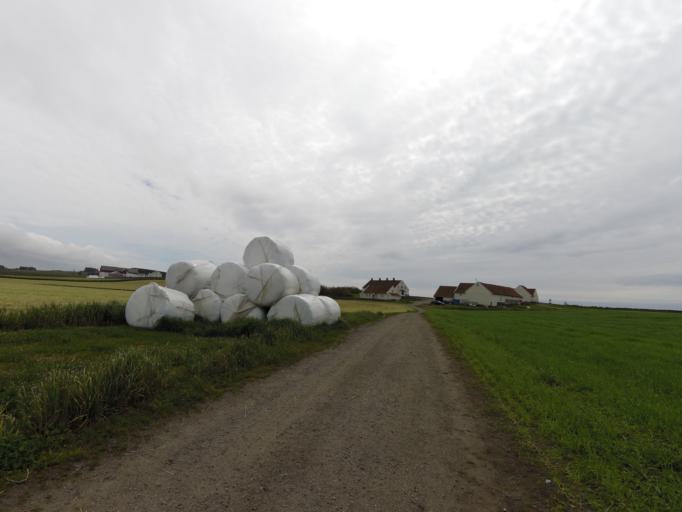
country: NO
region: Rogaland
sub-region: Ha
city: Naerbo
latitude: 58.6684
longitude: 5.5523
